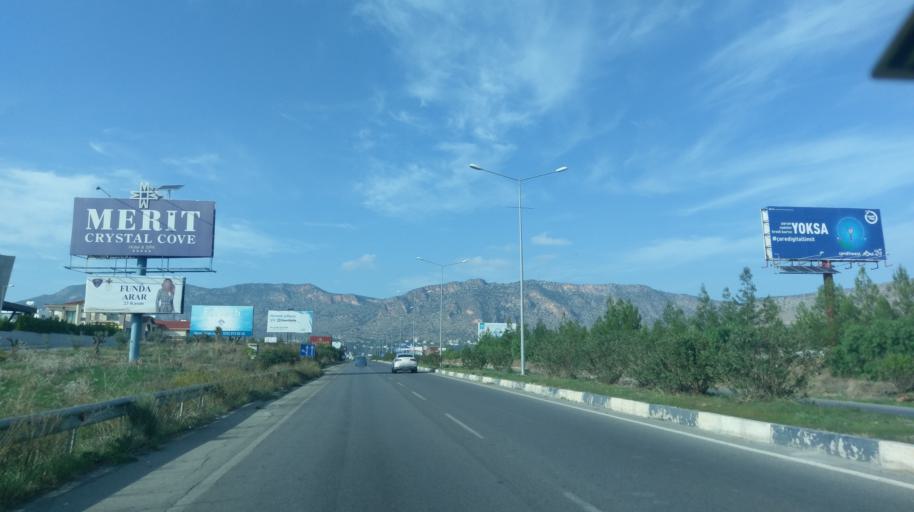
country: CY
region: Keryneia
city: Kyrenia
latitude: 35.2688
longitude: 33.2910
